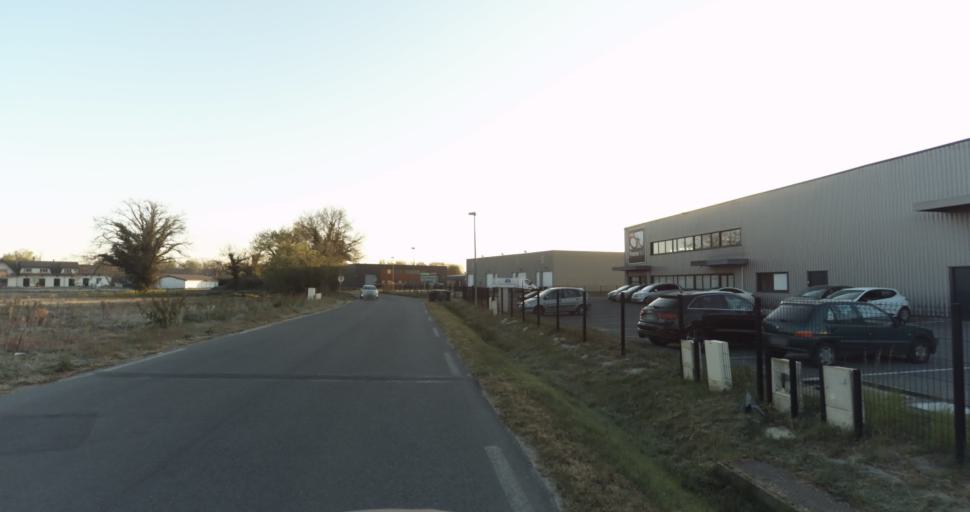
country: FR
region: Aquitaine
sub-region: Departement de la Gironde
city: Martignas-sur-Jalle
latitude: 44.8135
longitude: -0.7498
